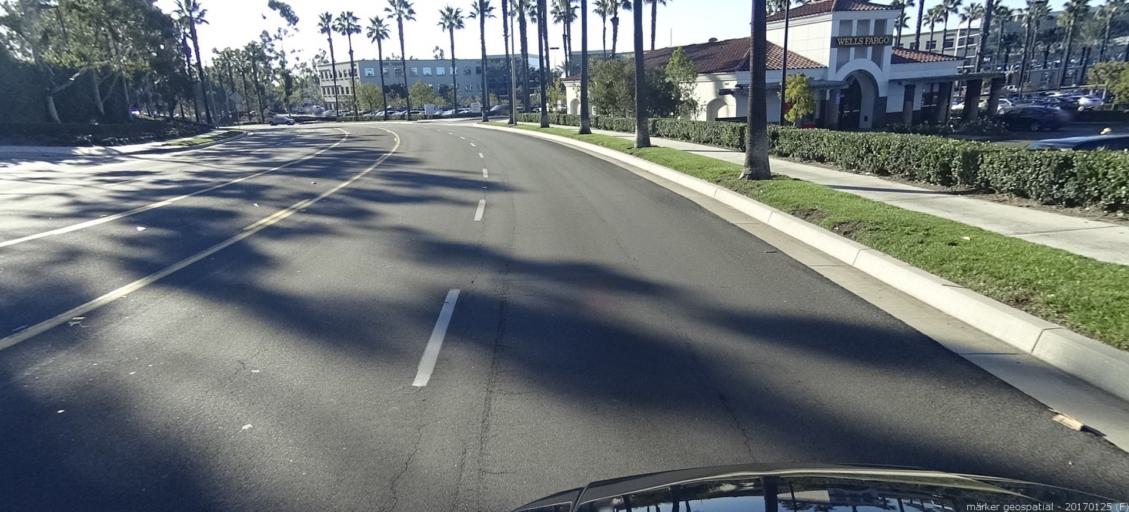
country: US
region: California
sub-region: Orange County
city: Foothill Ranch
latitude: 33.6772
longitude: -117.6662
